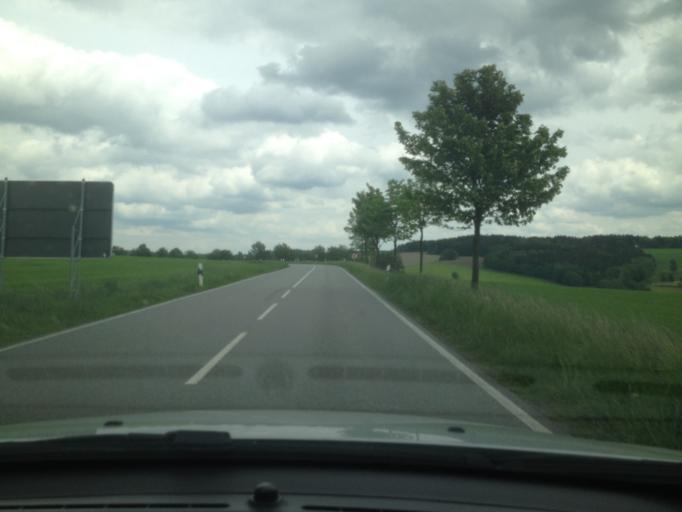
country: DE
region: Saxony
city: Lossnitz
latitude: 50.6462
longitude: 12.7483
